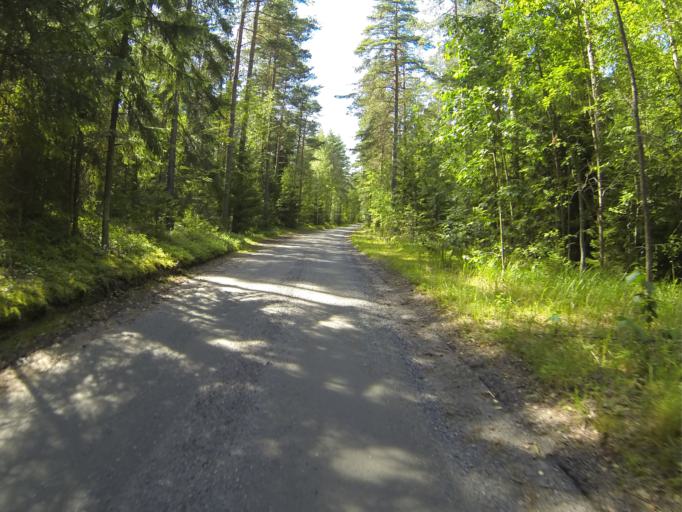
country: FI
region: Varsinais-Suomi
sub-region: Salo
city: Halikko
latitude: 60.2757
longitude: 22.9993
